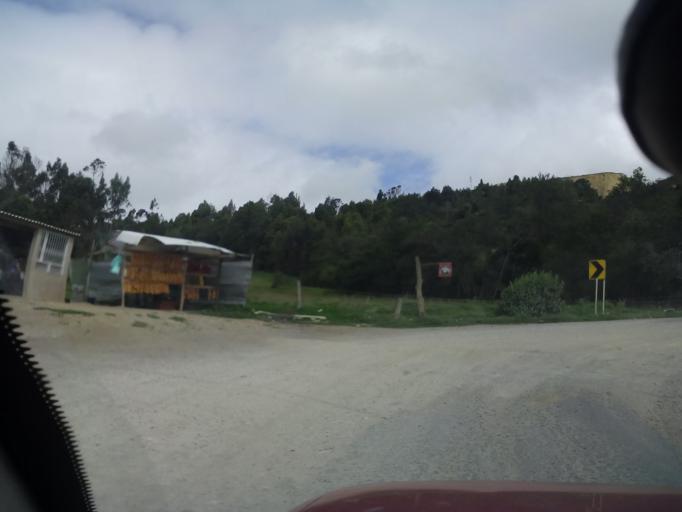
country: CO
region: Boyaca
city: Combita
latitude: 5.6308
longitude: -73.3416
